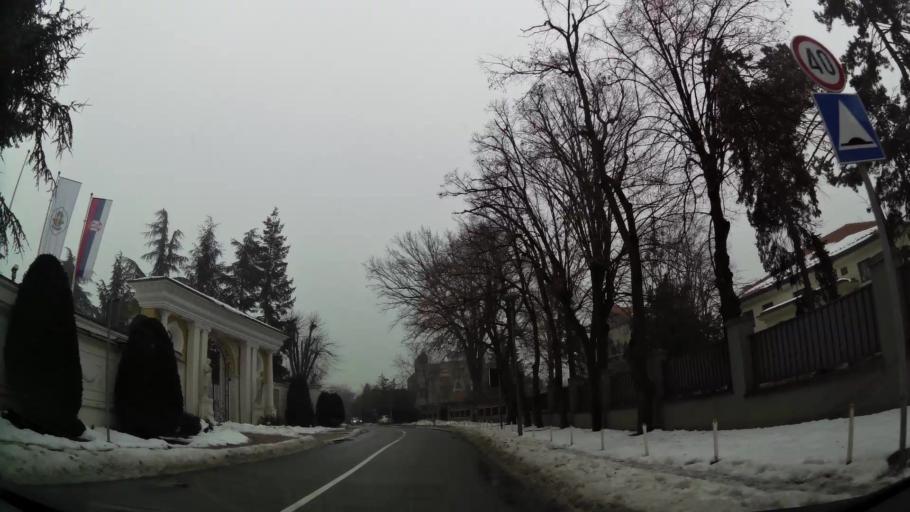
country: RS
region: Central Serbia
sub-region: Belgrade
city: Savski Venac
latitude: 44.7816
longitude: 20.4553
